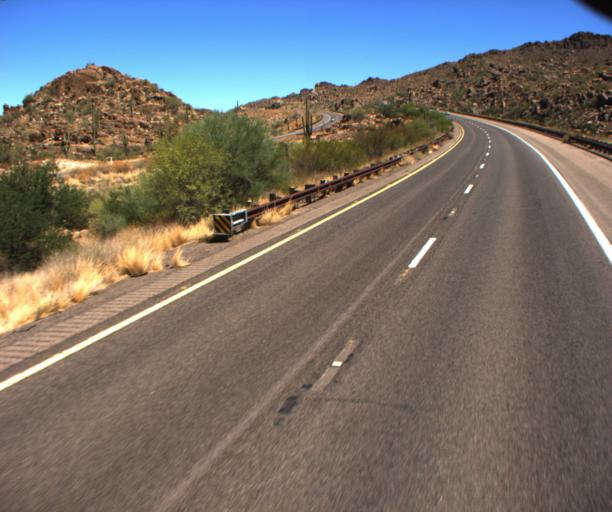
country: US
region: Arizona
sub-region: Maricopa County
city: Rio Verde
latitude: 33.6844
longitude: -111.4996
